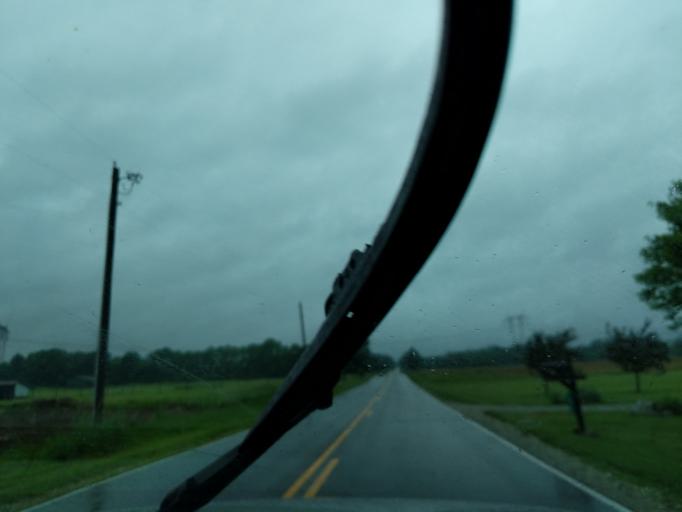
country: US
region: Indiana
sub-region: Madison County
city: Lapel
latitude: 40.0671
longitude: -85.8752
